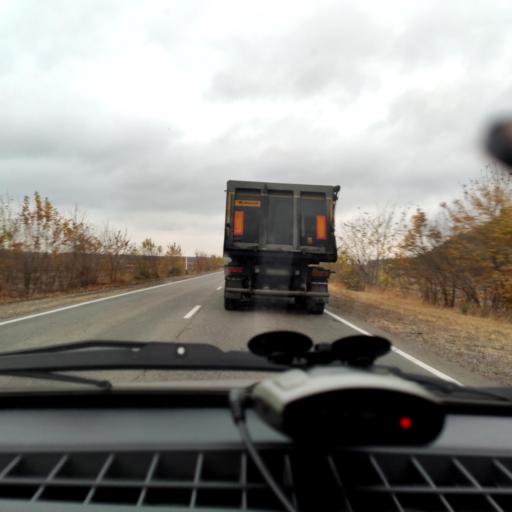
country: RU
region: Voronezj
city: Shilovo
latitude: 51.4420
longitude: 38.9960
